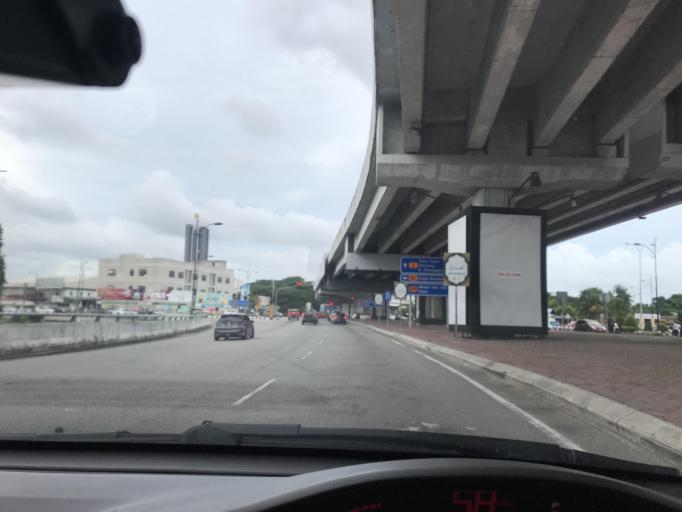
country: MY
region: Kelantan
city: Kota Bharu
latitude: 6.1156
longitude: 102.2352
